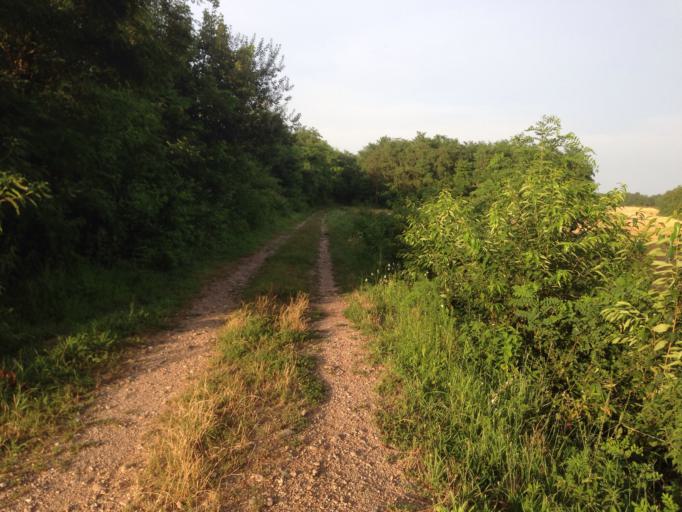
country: IT
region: Lombardy
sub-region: Citta metropolitana di Milano
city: Nosate
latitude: 45.5516
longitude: 8.7469
